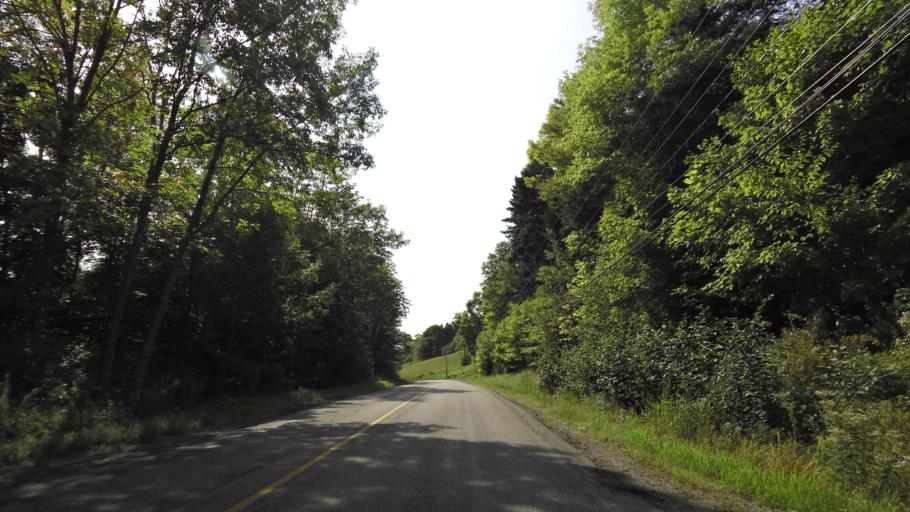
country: CA
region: New Brunswick
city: Hampton
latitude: 45.5442
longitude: -65.8481
